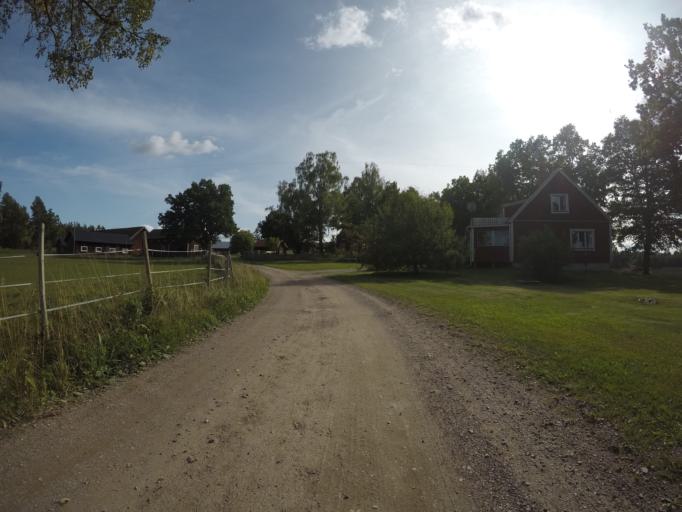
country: SE
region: Vaestmanland
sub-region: Hallstahammars Kommun
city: Kolback
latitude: 59.5373
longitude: 16.3307
